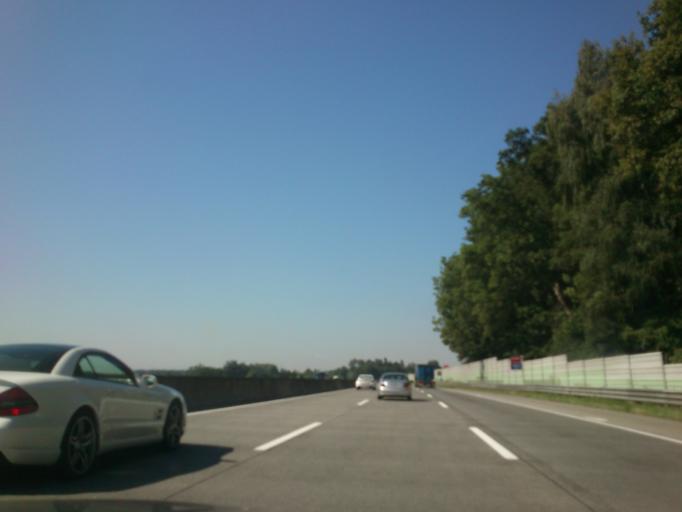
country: AT
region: Upper Austria
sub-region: Politischer Bezirk Linz-Land
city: Horsching
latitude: 48.1761
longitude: 14.1786
